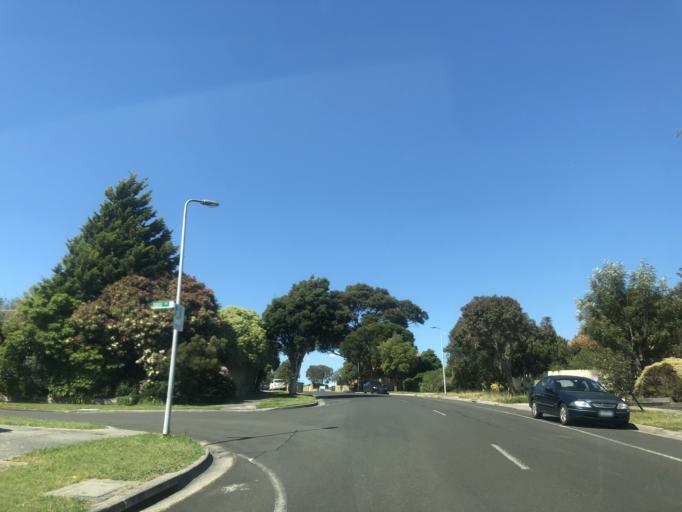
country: AU
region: Victoria
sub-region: Casey
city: Endeavour Hills
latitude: -37.9900
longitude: 145.2629
